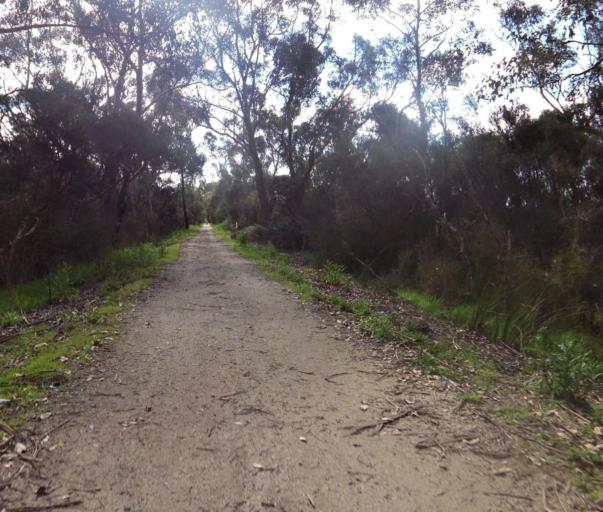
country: AU
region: Victoria
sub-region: Bass Coast
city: North Wonthaggi
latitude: -38.5837
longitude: 146.0352
